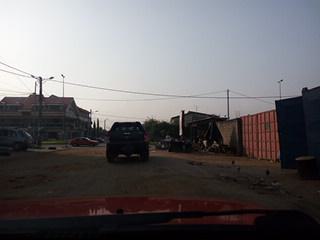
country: CI
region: Lagunes
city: Abobo
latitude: 5.3922
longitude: -3.9815
